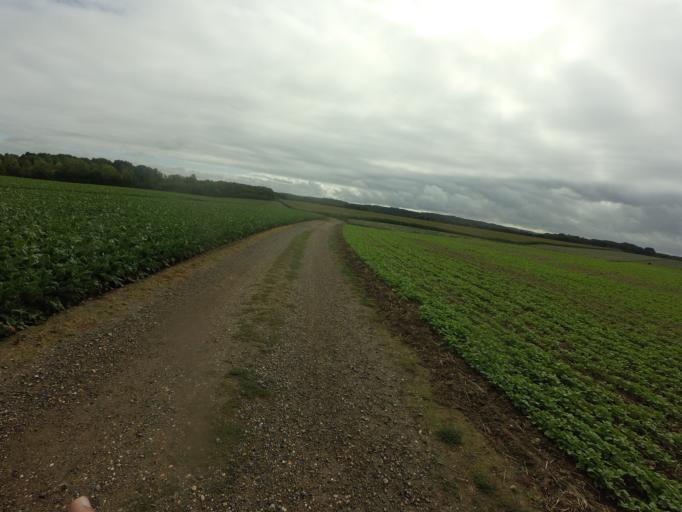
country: NL
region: Limburg
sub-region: Eijsden-Margraten
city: Margraten
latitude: 50.7871
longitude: 5.8418
